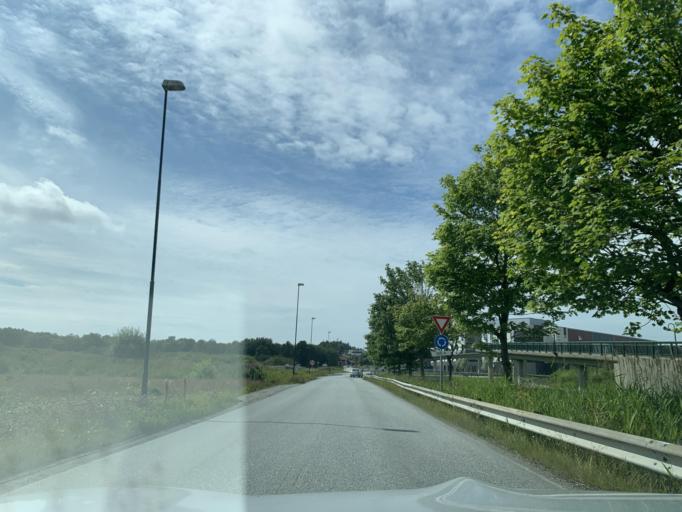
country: NO
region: Rogaland
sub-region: Sola
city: Sola
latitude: 58.8940
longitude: 5.6840
